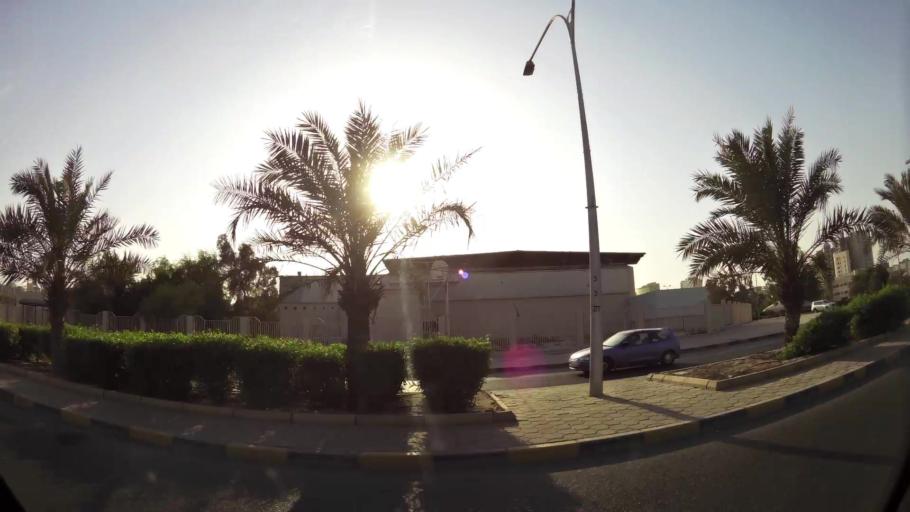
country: KW
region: Muhafazat Hawalli
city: As Salimiyah
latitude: 29.3388
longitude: 48.0790
